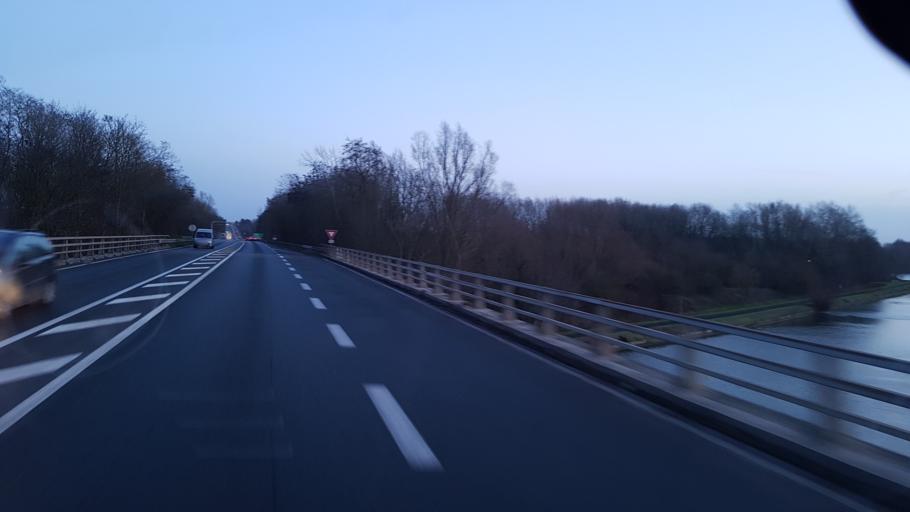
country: FR
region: Nord-Pas-de-Calais
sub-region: Departement du Nord
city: Lambres-lez-Douai
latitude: 50.3542
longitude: 3.0519
